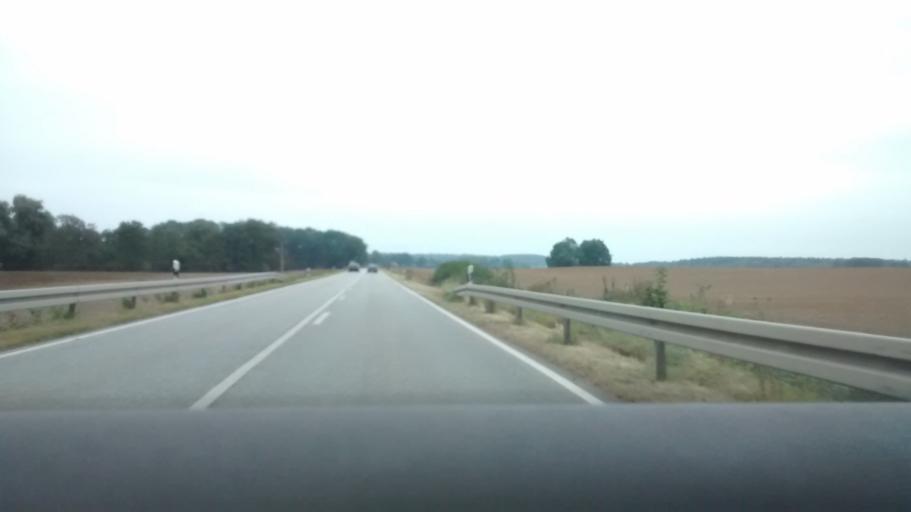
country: DE
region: Mecklenburg-Vorpommern
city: Mecklenburg
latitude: 53.8048
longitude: 11.4343
